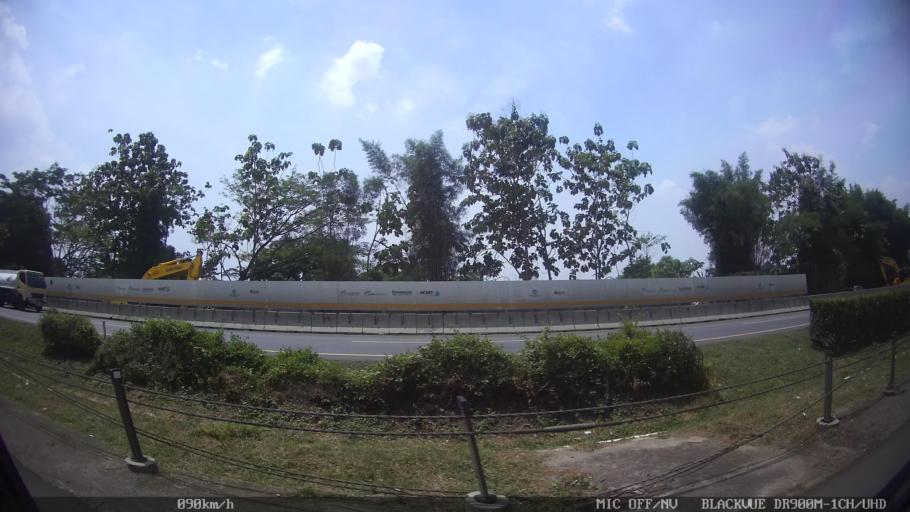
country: ID
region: Banten
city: Serang
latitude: -6.1368
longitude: 106.2168
